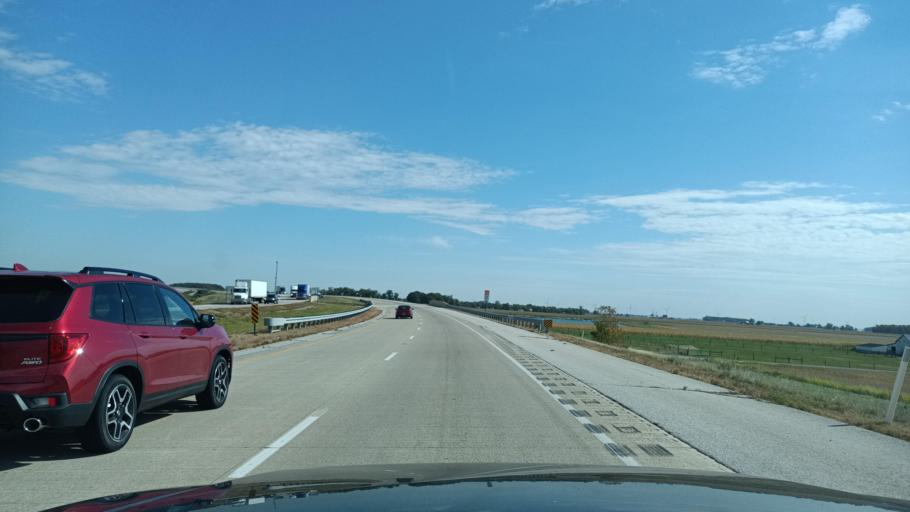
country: US
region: Indiana
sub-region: Allen County
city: Woodburn
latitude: 41.1219
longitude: -84.8883
